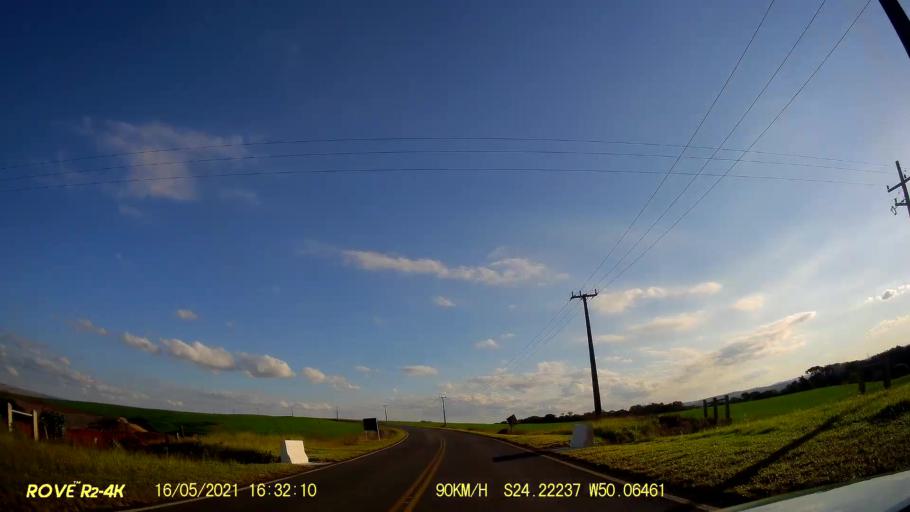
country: BR
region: Parana
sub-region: Pirai Do Sul
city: Pirai do Sul
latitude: -24.2230
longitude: -50.0642
